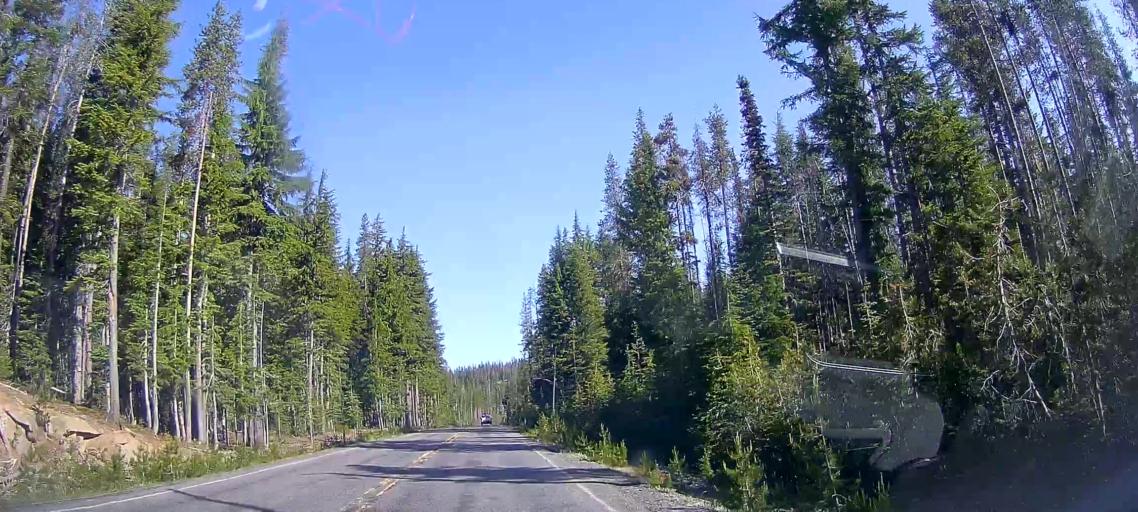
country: US
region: Oregon
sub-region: Jackson County
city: Shady Cove
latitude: 42.8381
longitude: -122.1444
